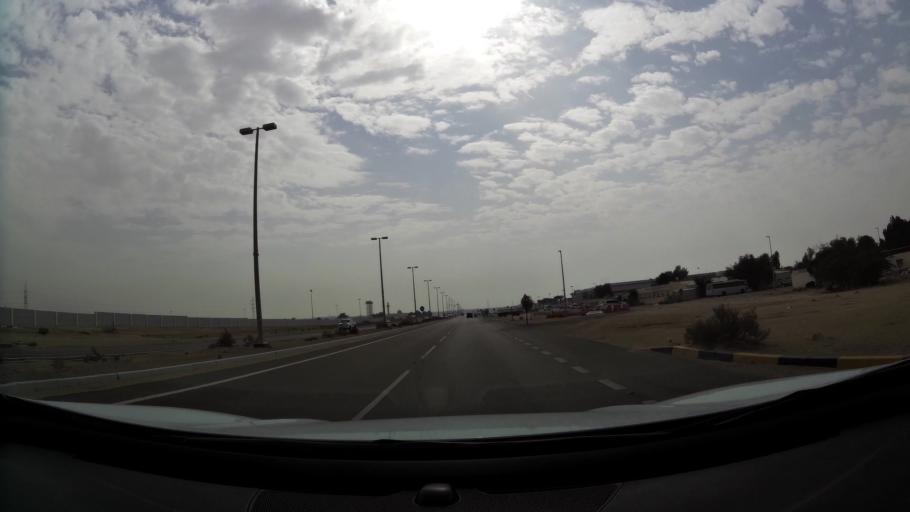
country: AE
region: Abu Dhabi
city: Abu Dhabi
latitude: 24.2890
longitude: 54.6623
